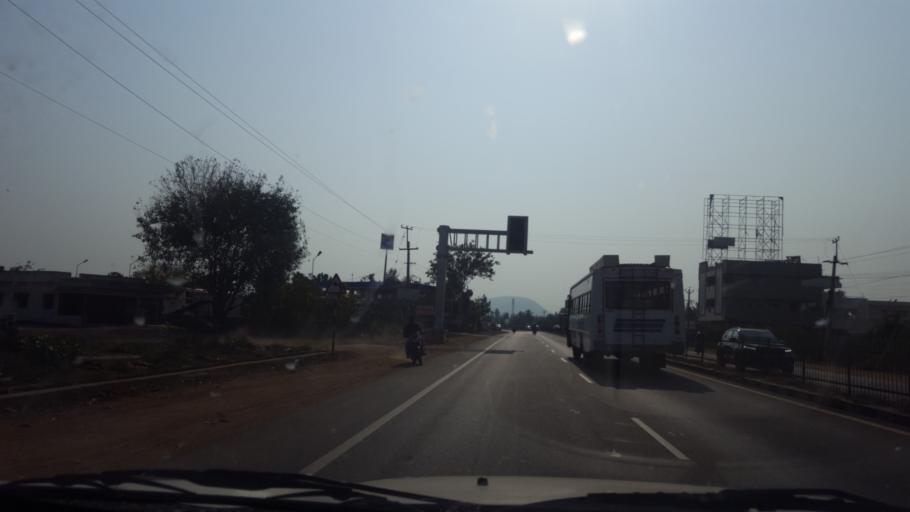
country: IN
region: Andhra Pradesh
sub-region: Vishakhapatnam
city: Anakapalle
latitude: 17.6747
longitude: 82.9728
